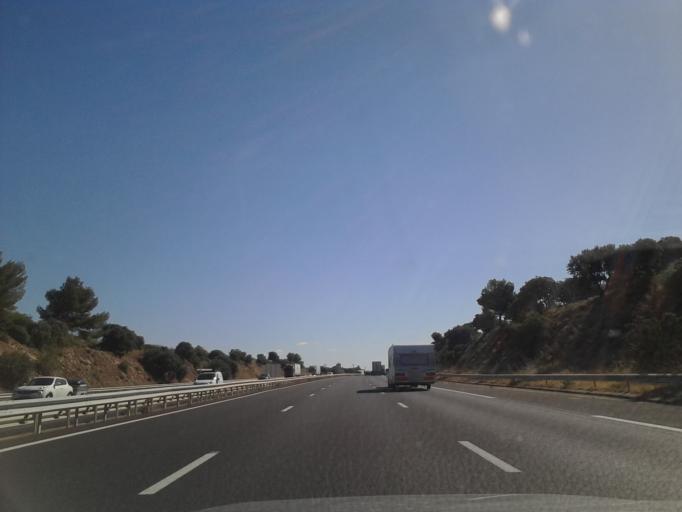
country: FR
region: Languedoc-Roussillon
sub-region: Departement de l'Herault
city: Vendres
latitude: 43.2985
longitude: 3.2045
